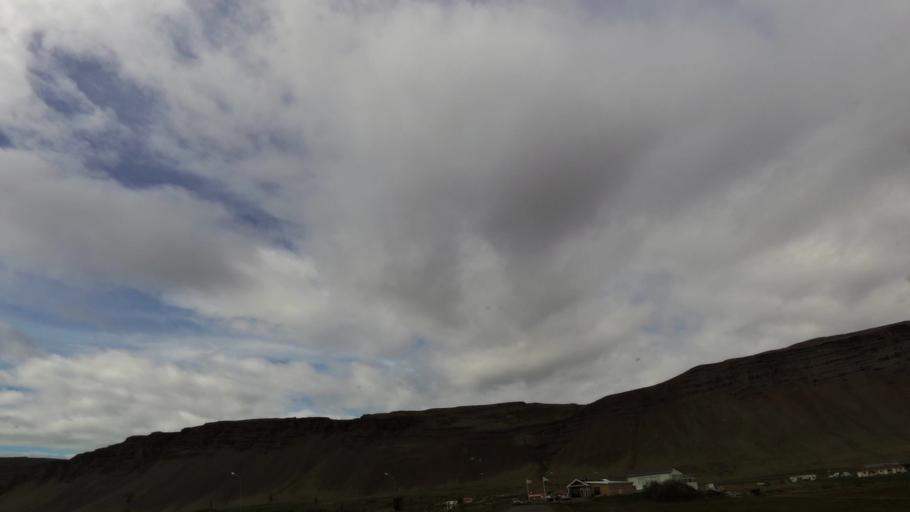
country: IS
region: West
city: Stykkisholmur
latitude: 65.4501
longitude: -22.2012
